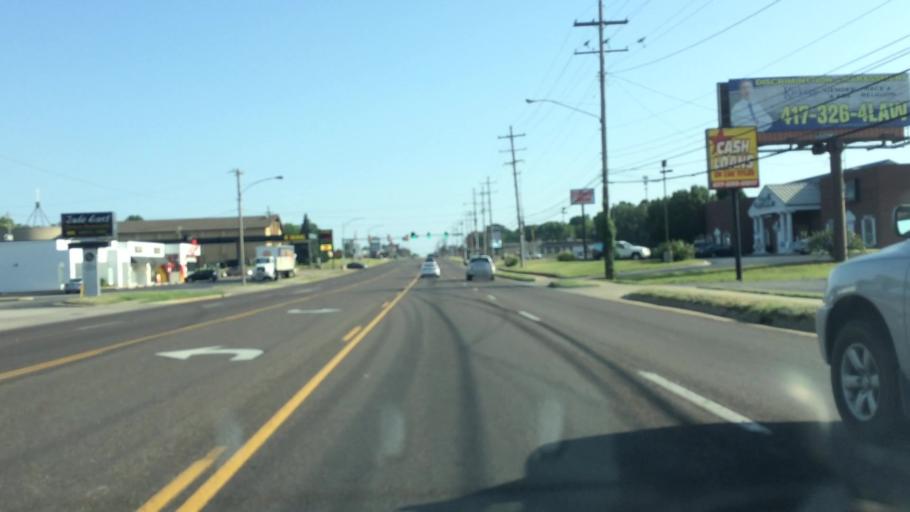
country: US
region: Missouri
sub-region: Greene County
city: Springfield
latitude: 37.1697
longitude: -93.2954
